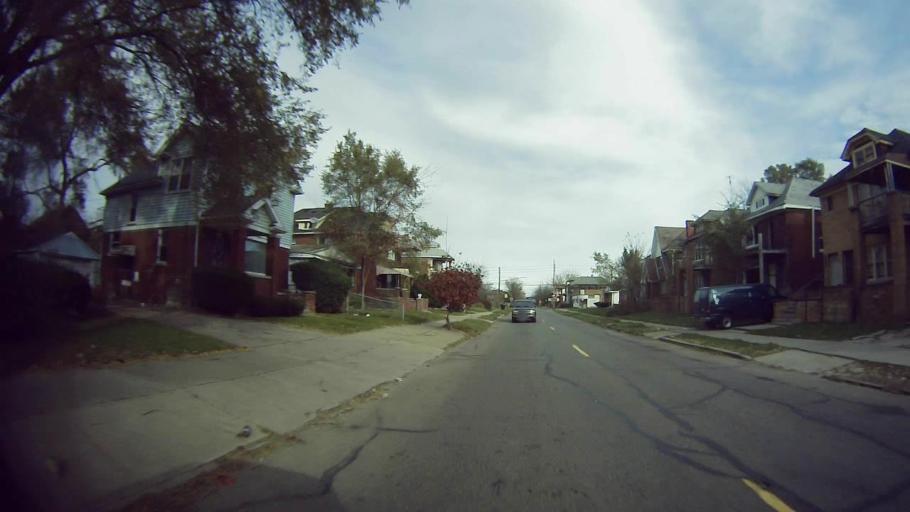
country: US
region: Michigan
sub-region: Wayne County
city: Highland Park
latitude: 42.3791
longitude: -83.1303
